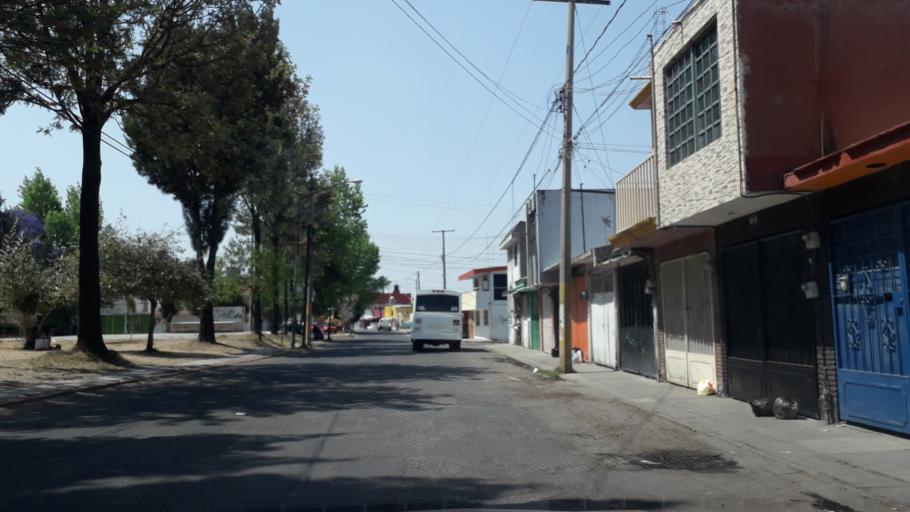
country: MX
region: Puebla
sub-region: Cuautlancingo
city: Sanctorum
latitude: 19.0901
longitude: -98.2220
